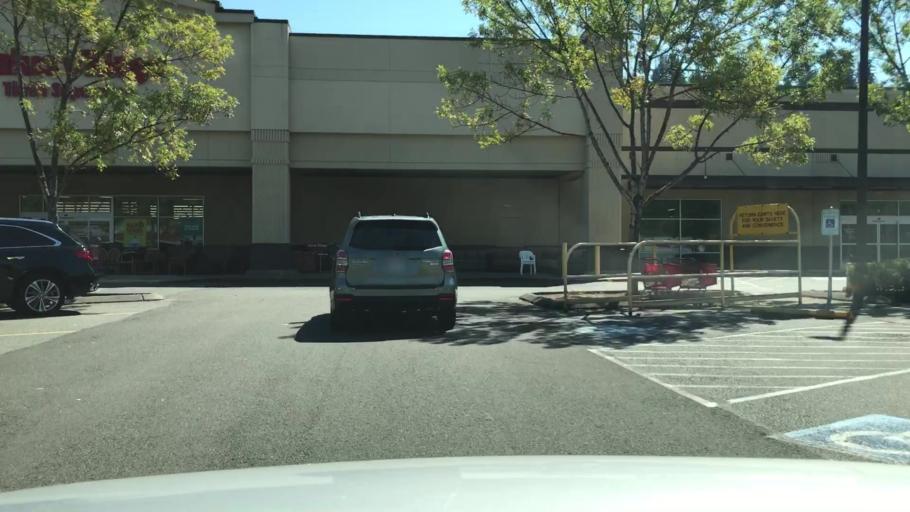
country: US
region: Washington
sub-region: King County
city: Issaquah
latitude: 47.5526
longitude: -122.0430
